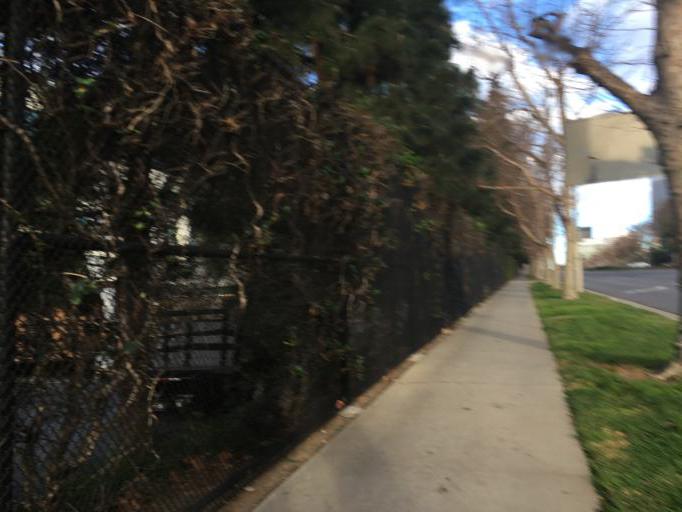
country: US
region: California
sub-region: Los Angeles County
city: Century City
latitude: 34.0515
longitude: -118.4092
